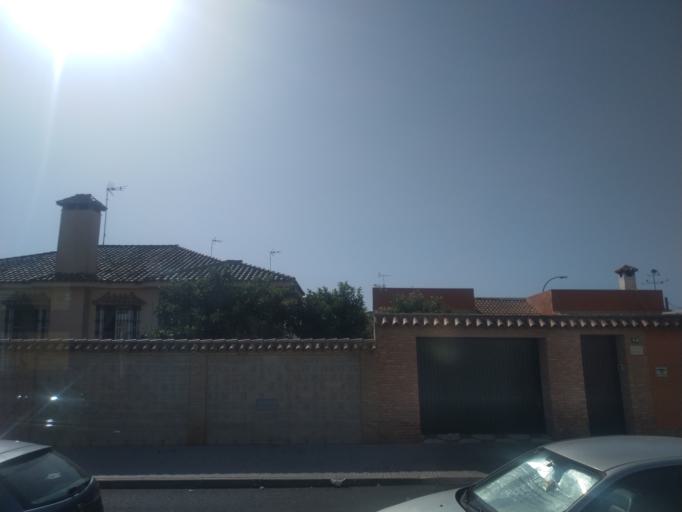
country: ES
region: Andalusia
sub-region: Provincia de Cadiz
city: San Fernando
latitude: 36.4535
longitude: -6.2112
